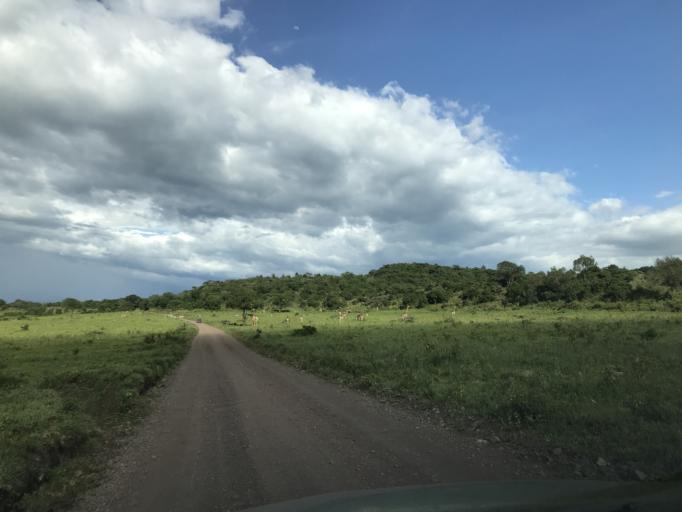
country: TZ
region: Arusha
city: Nkoaranga
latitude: -3.2389
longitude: 36.8636
